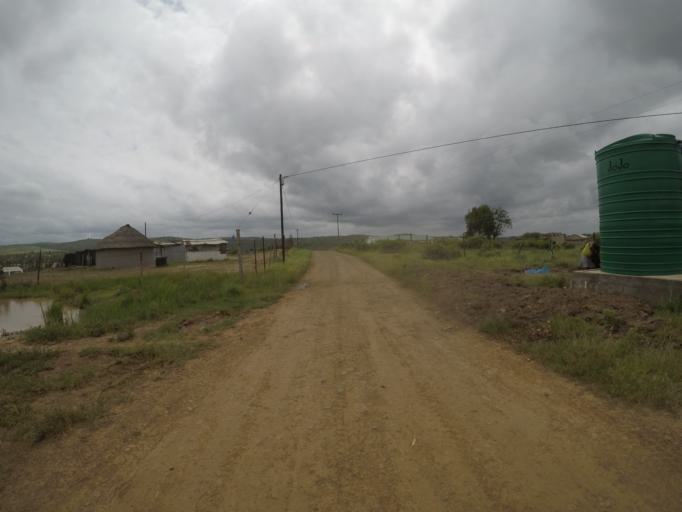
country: ZA
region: KwaZulu-Natal
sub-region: uThungulu District Municipality
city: Empangeni
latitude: -28.5992
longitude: 31.8325
